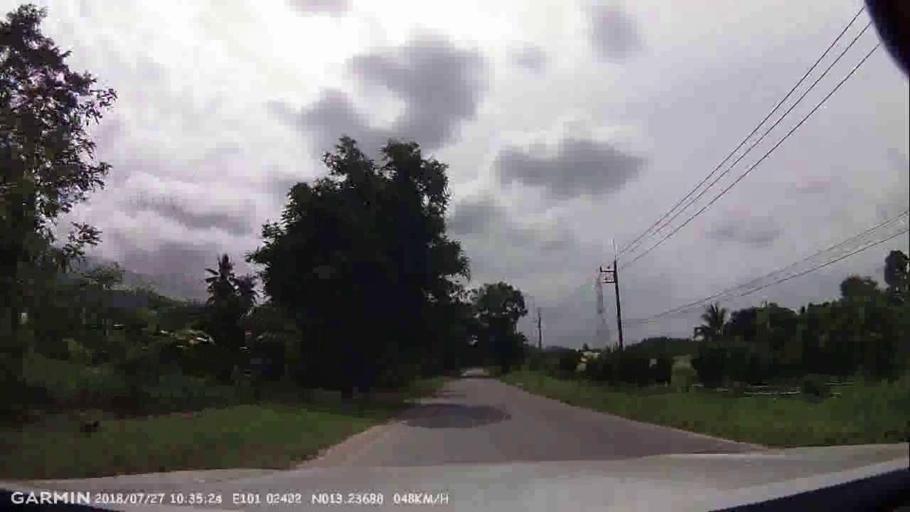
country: TH
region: Chon Buri
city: Si Racha
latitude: 13.2369
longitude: 101.0243
